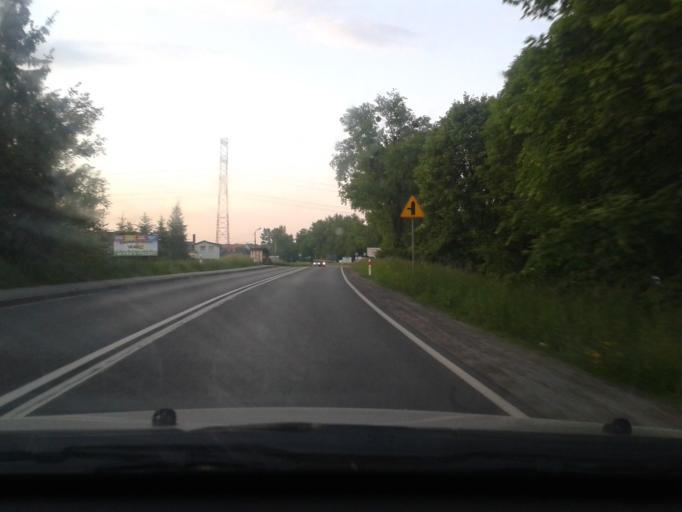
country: PL
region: Lesser Poland Voivodeship
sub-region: Powiat oswiecimski
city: Rajsko
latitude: 50.0168
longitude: 19.1952
